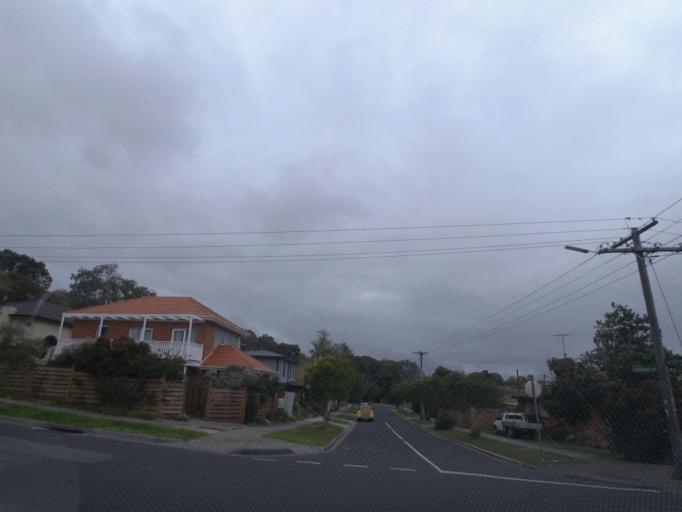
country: AU
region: Victoria
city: Ashburton
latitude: -37.8702
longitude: 145.0780
